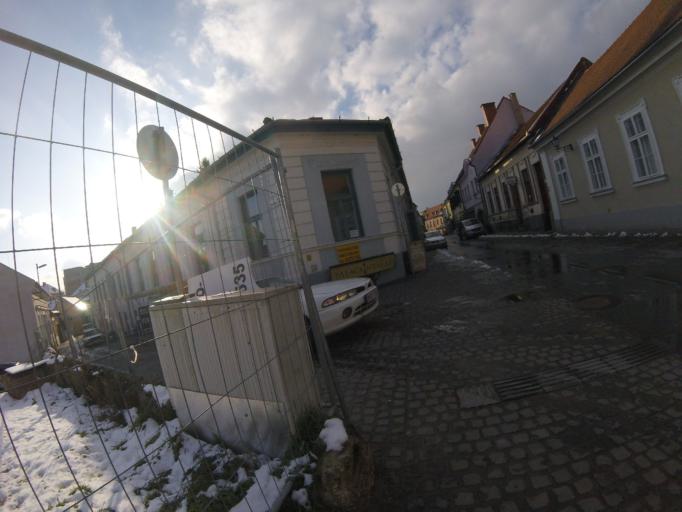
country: HU
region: Heves
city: Eger
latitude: 47.9029
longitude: 20.3798
